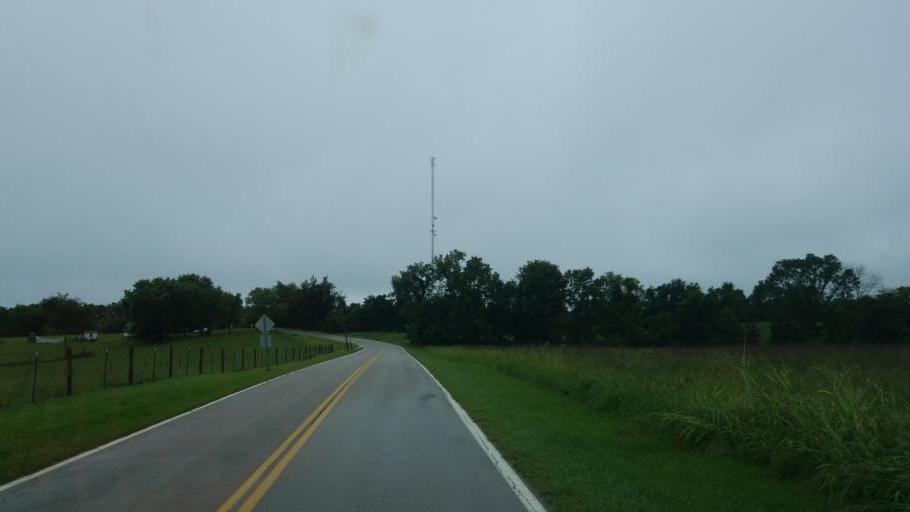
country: US
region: Ohio
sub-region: Adams County
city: West Union
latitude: 38.7331
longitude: -83.5174
